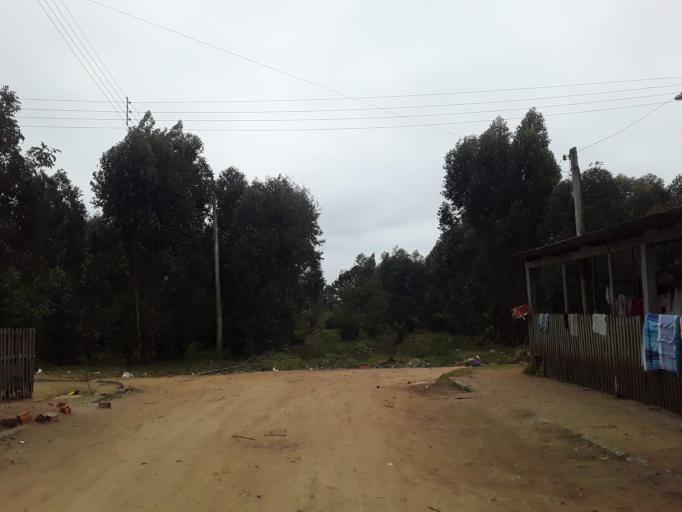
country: BR
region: Rio Grande do Sul
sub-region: Sao Lourenco Do Sul
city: Sao Lourenco do Sul
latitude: -31.3404
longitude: -51.9908
